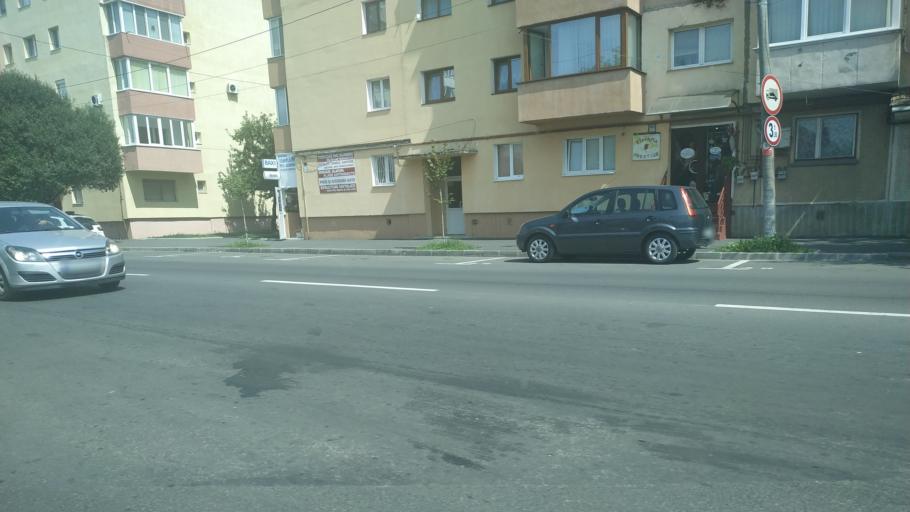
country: RO
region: Brasov
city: Fogarasch
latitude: 45.8392
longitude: 24.9672
